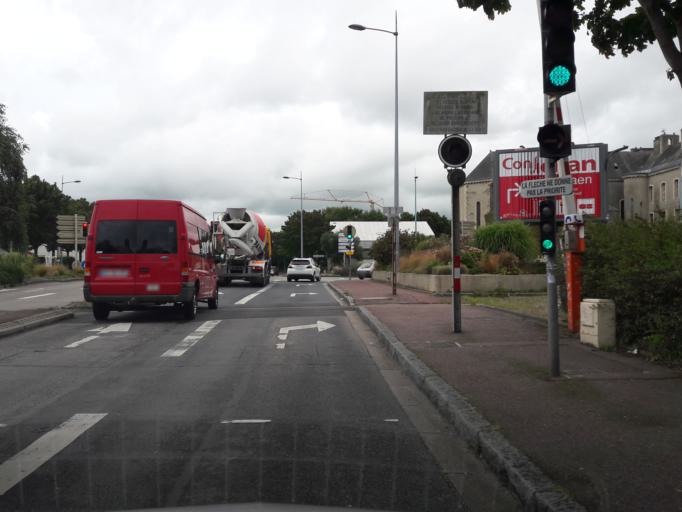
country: FR
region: Lower Normandy
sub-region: Departement de la Manche
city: Cherbourg-Octeville
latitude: 49.6335
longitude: -1.6182
